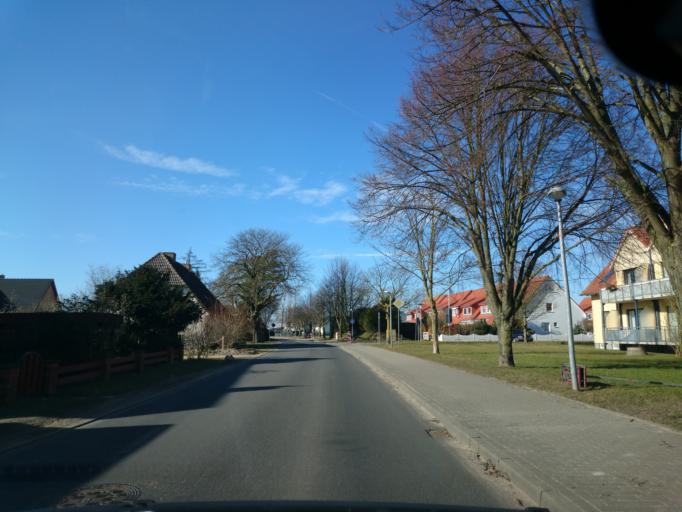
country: DE
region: Mecklenburg-Vorpommern
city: Borgerende-Rethwisch
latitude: 54.1412
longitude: 11.9340
